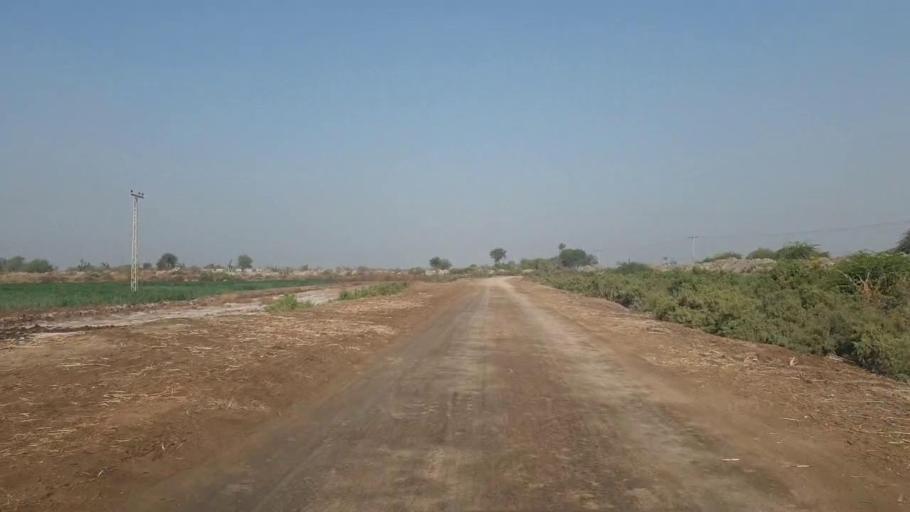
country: PK
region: Sindh
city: Mirwah Gorchani
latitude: 25.3726
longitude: 69.1872
